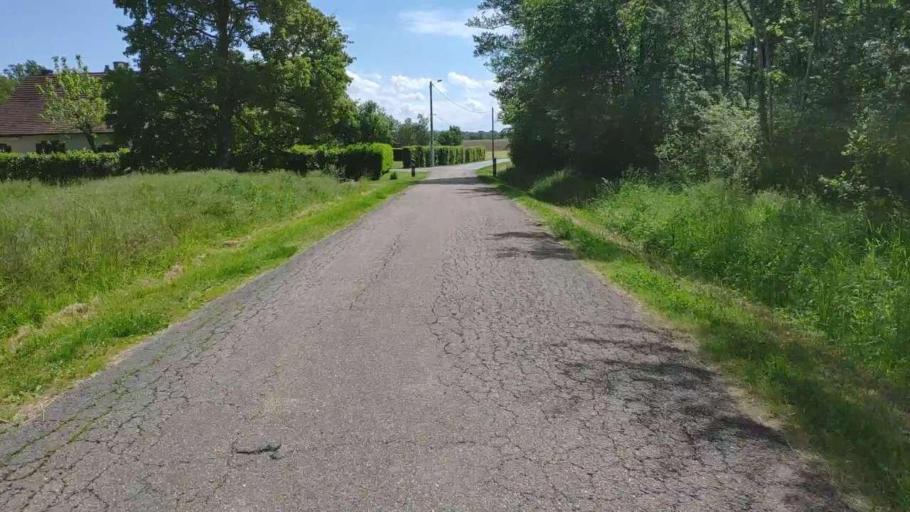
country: FR
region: Franche-Comte
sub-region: Departement du Jura
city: Bletterans
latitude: 46.7089
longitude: 5.4164
